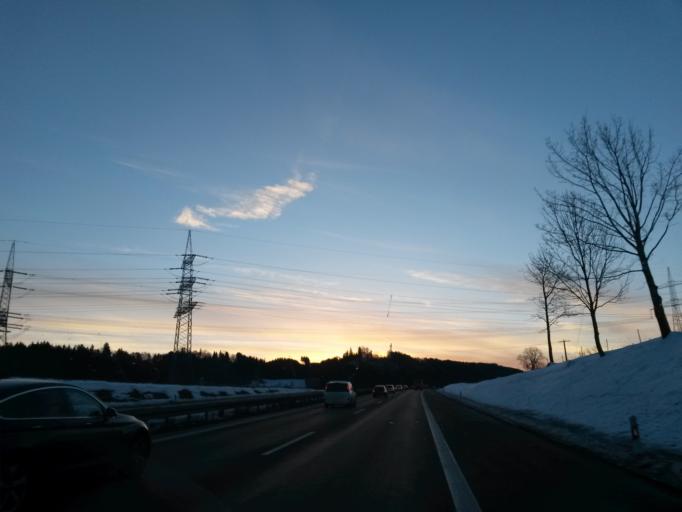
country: DE
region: Bavaria
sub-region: Swabia
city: Wolfertschwenden
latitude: 47.8675
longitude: 10.2638
